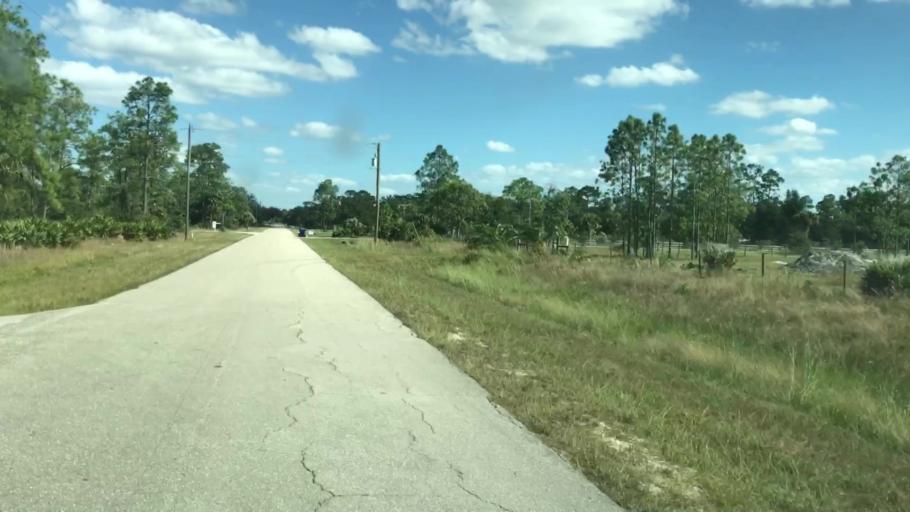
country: US
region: Florida
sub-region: Lee County
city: Alva
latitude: 26.6839
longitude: -81.5752
